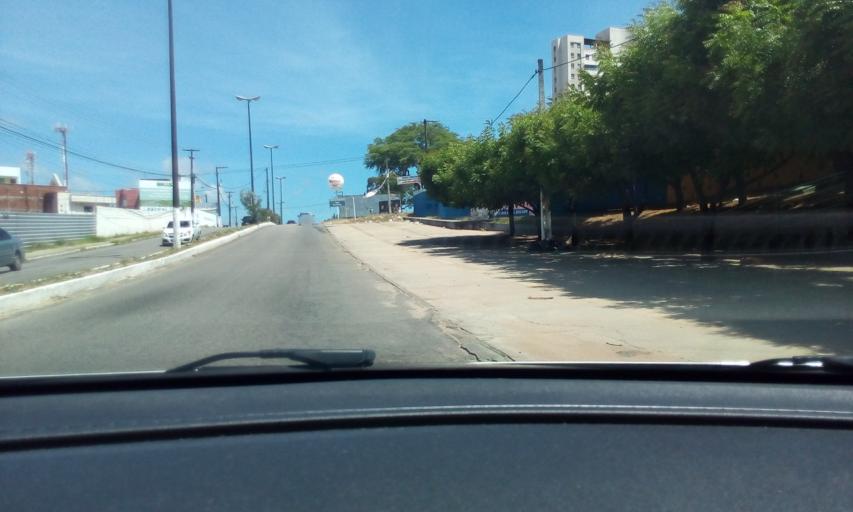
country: BR
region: Rio Grande do Norte
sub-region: Parnamirim
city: Parnamirim
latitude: -5.8826
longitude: -35.2005
